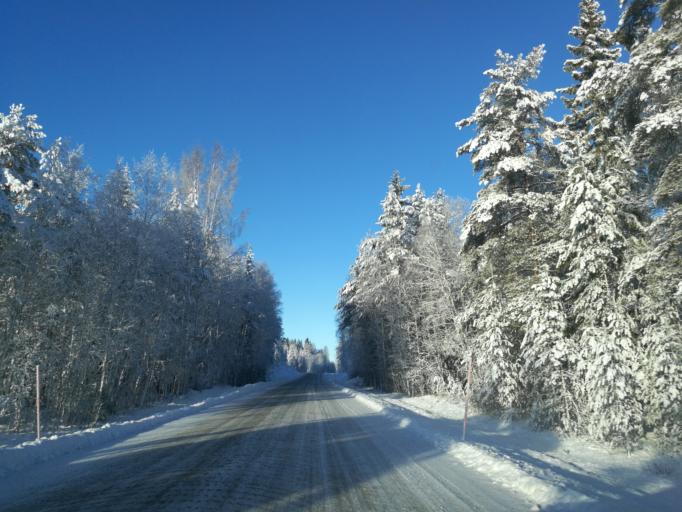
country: NO
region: Hedmark
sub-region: Grue
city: Kirkenaer
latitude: 60.5464
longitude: 12.5426
